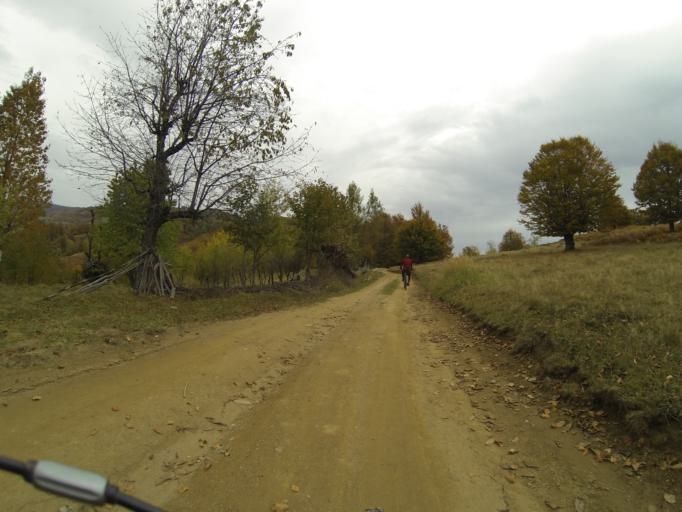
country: RO
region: Gorj
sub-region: Comuna Tismana
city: Sohodol
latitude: 45.1227
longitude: 22.8564
